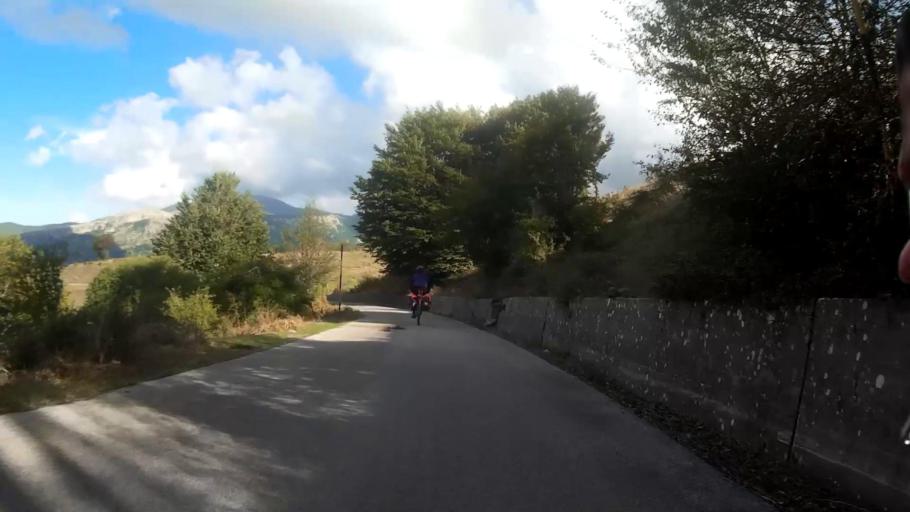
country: IT
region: Basilicate
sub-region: Provincia di Potenza
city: Viggianello
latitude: 39.9581
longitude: 16.1403
